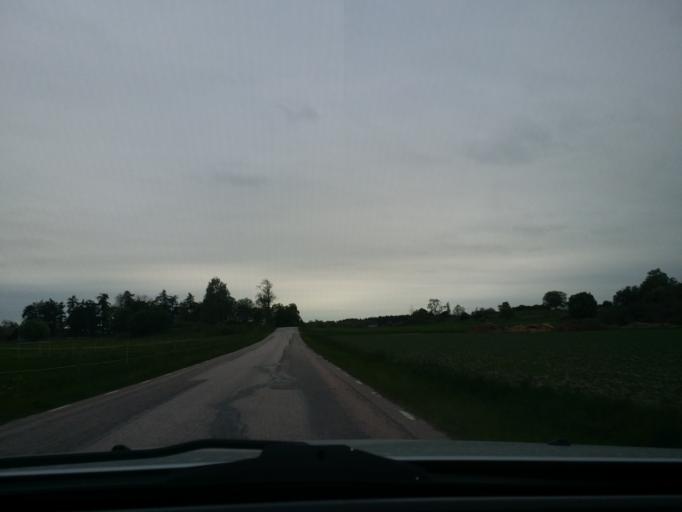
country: SE
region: Vaestmanland
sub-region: Hallstahammars Kommun
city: Kolback
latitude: 59.5387
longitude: 16.3031
